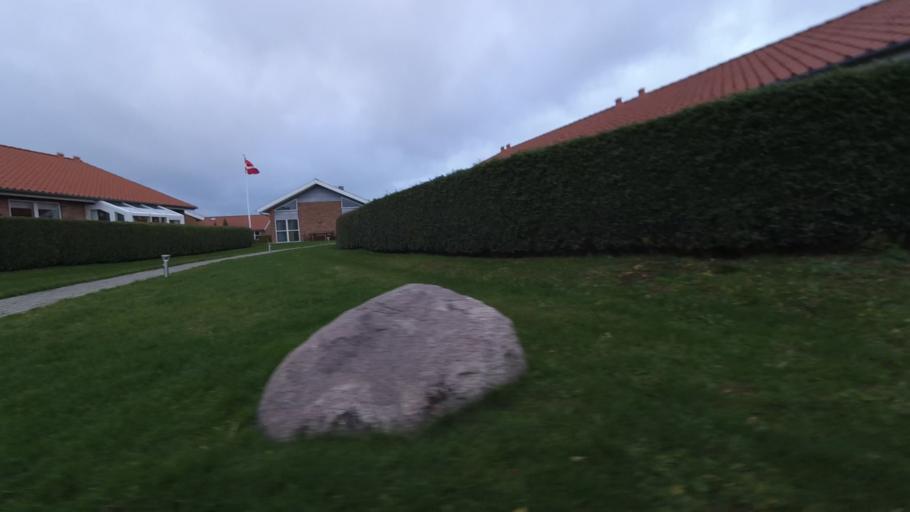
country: DK
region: Central Jutland
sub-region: Arhus Kommune
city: Marslet
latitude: 56.1033
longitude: 10.1775
